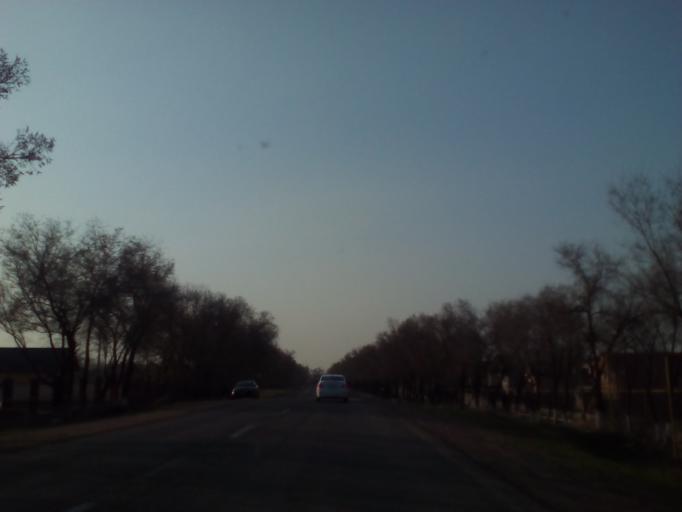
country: KZ
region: Almaty Oblysy
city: Burunday
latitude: 43.1782
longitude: 76.5203
